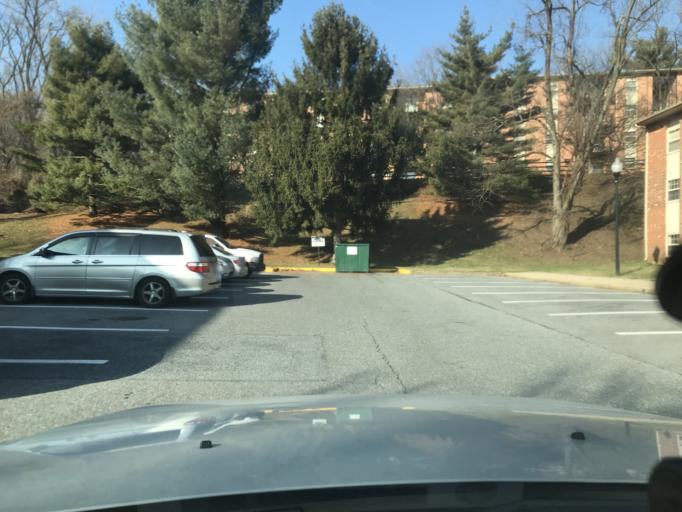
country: US
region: Maryland
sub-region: Baltimore County
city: Owings Mills
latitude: 39.4152
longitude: -76.7912
